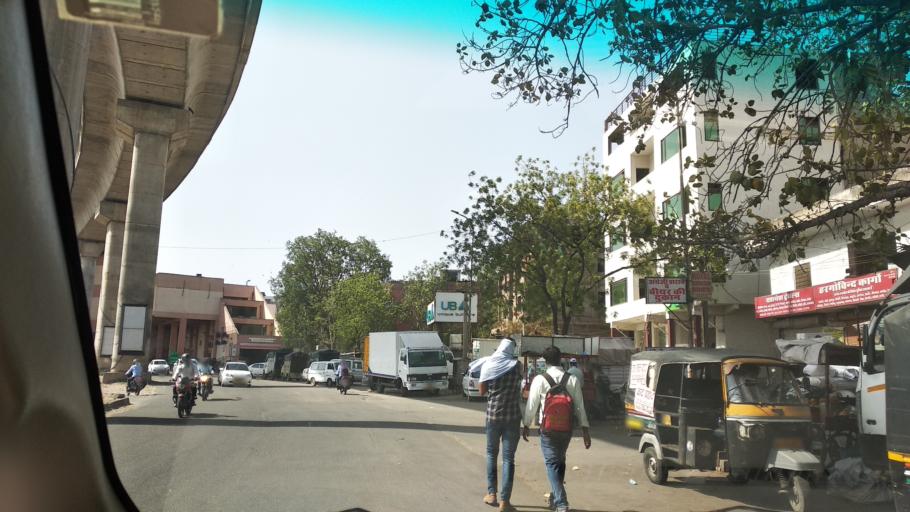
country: IN
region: Rajasthan
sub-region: Jaipur
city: Jaipur
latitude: 26.9165
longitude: 75.7910
